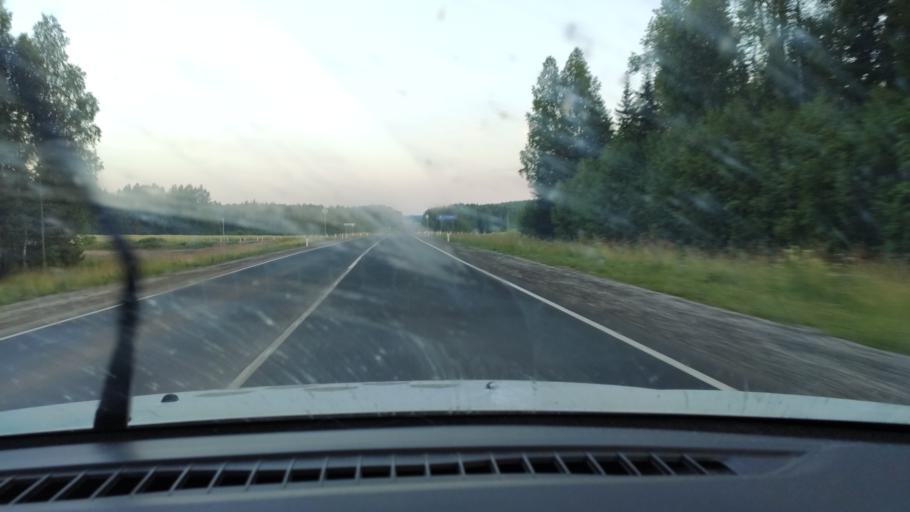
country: RU
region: Perm
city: Siva
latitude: 58.3985
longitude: 54.5048
